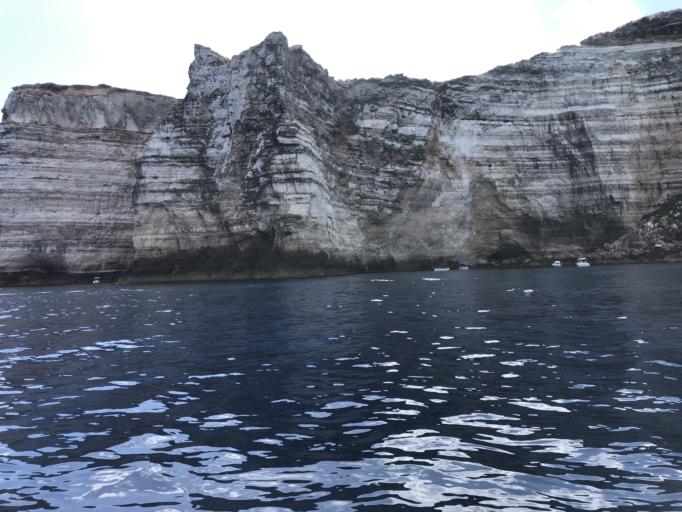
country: IT
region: Sicily
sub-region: Agrigento
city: Lampedusa
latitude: 35.5283
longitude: 12.5237
